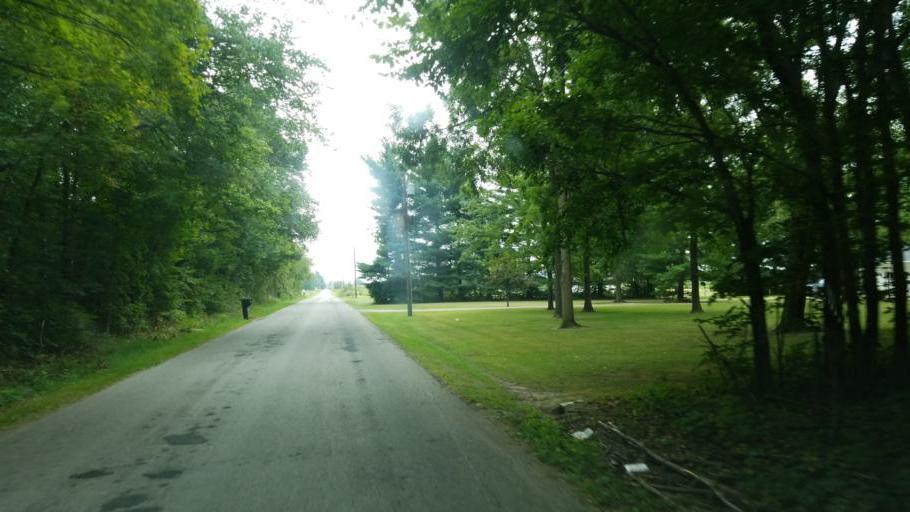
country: US
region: Ohio
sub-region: Morrow County
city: Mount Gilead
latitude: 40.6334
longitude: -82.8417
